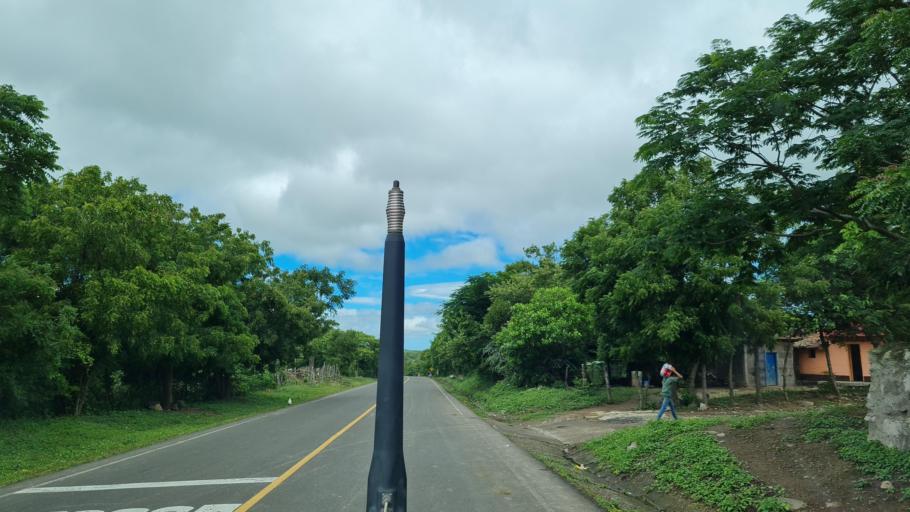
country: NI
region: Matagalpa
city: Terrabona
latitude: 12.5856
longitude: -85.9699
